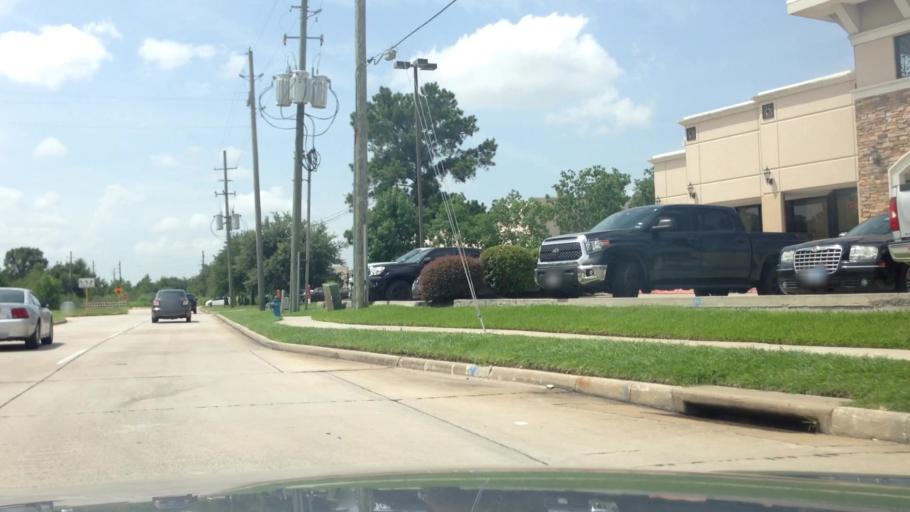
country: US
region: Texas
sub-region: Harris County
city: Jersey Village
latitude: 29.9289
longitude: -95.5439
